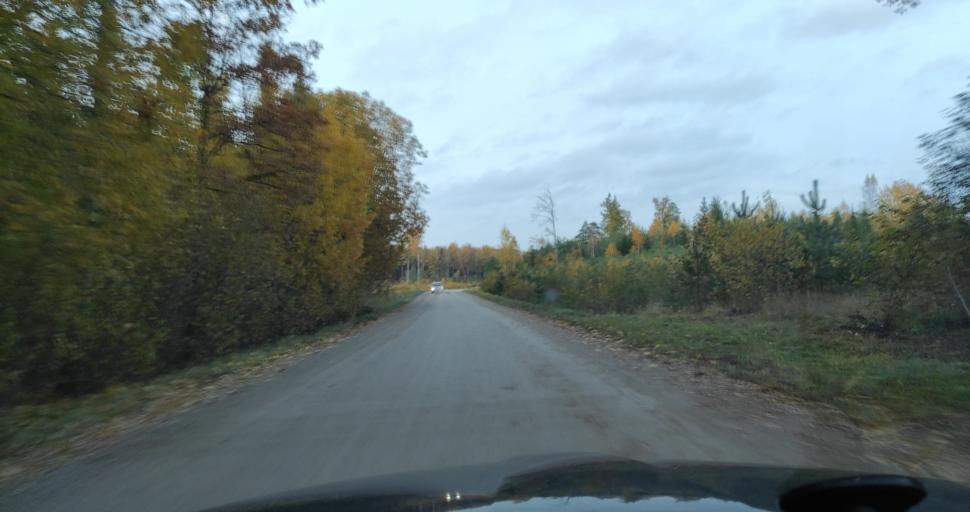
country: LV
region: Aizpute
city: Aizpute
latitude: 56.6716
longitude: 21.7916
